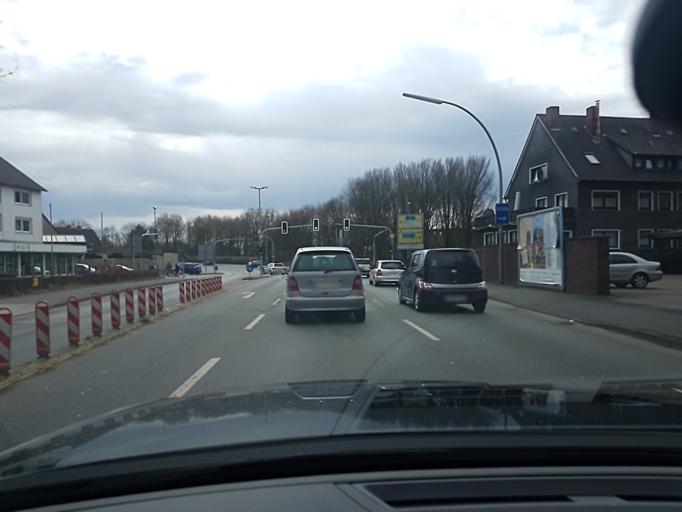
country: DE
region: North Rhine-Westphalia
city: Kamen
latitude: 51.5928
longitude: 7.6537
